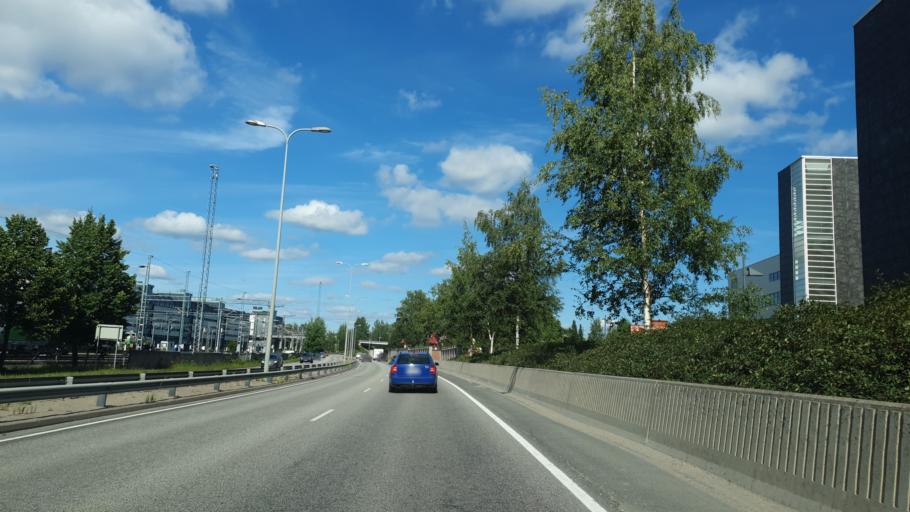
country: FI
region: Central Finland
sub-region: Jyvaeskylae
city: Jyvaeskylae
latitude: 62.2414
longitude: 25.7573
